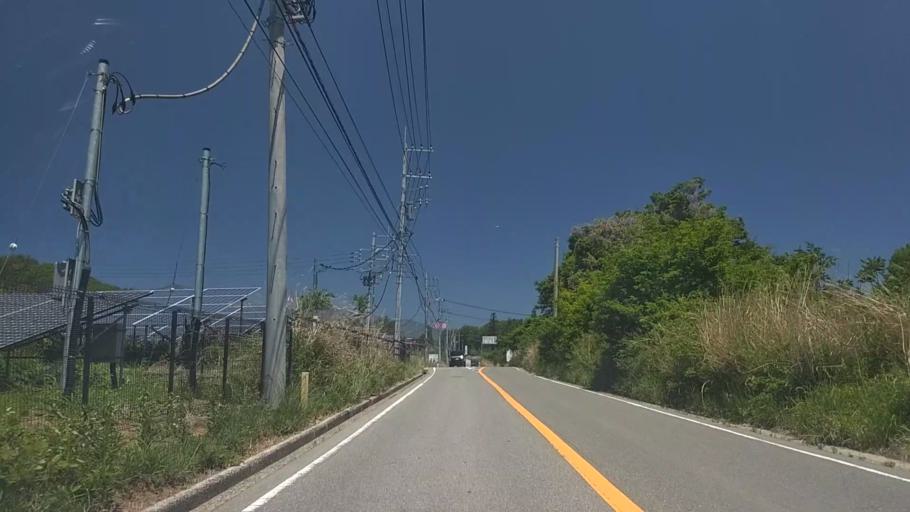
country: JP
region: Yamanashi
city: Nirasaki
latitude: 35.8504
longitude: 138.4321
